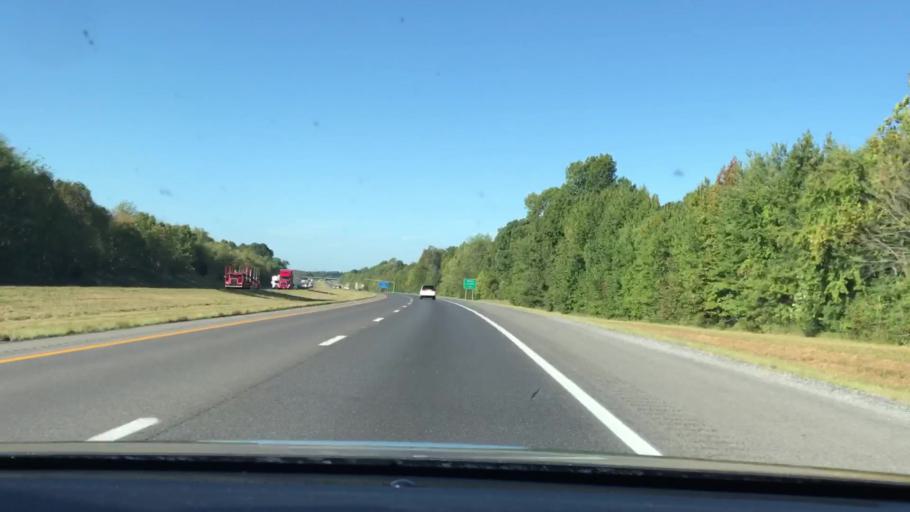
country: US
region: Kentucky
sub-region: Lyon County
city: Eddyville
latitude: 37.0683
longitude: -88.1612
